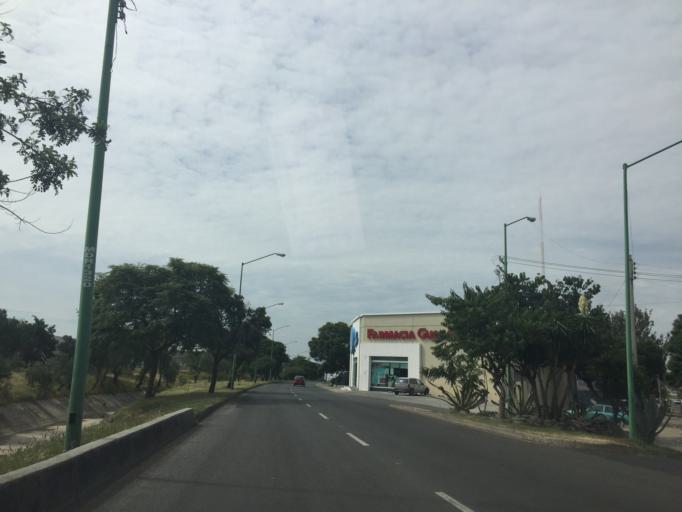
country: MX
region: Guanajuato
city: Leon
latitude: 21.1019
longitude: -101.6621
